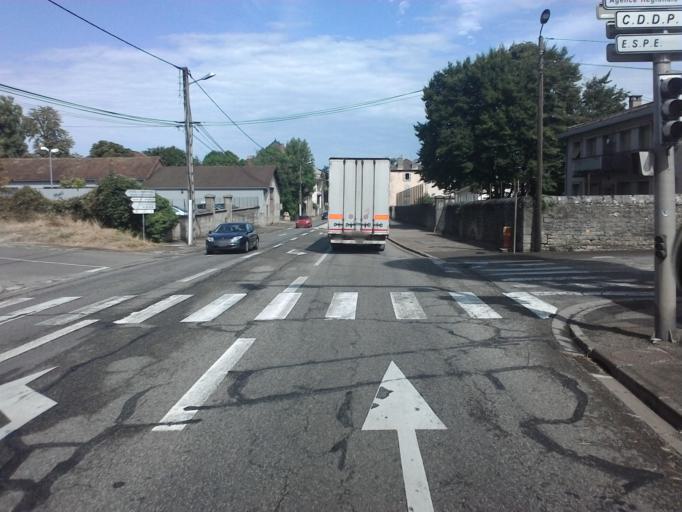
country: FR
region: Franche-Comte
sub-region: Departement du Jura
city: Lons-le-Saunier
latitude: 46.6705
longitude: 5.5457
